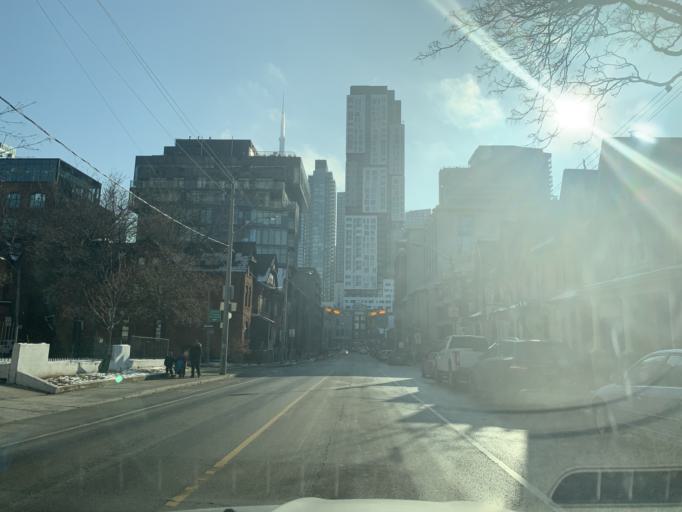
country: CA
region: Ontario
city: Toronto
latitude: 43.6513
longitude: -79.3928
